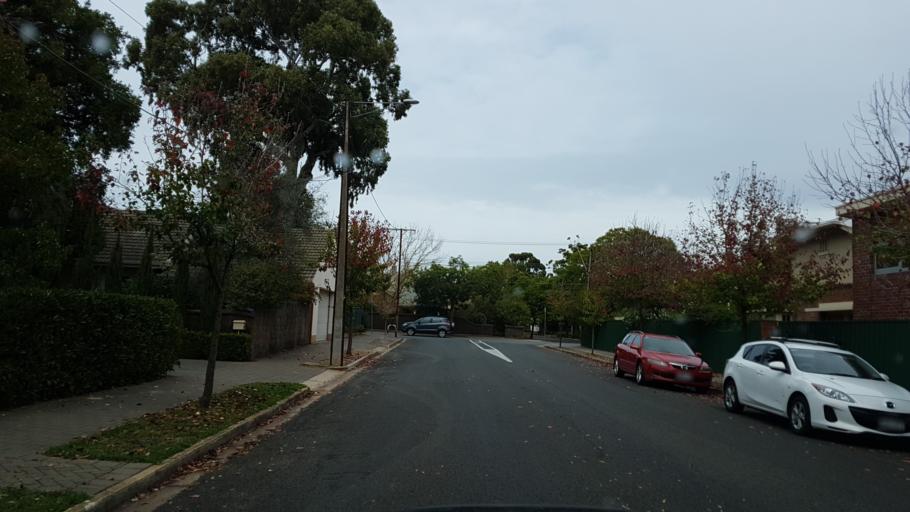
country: AU
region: South Australia
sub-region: Mitcham
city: Hawthorn
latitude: -34.9730
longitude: 138.6063
